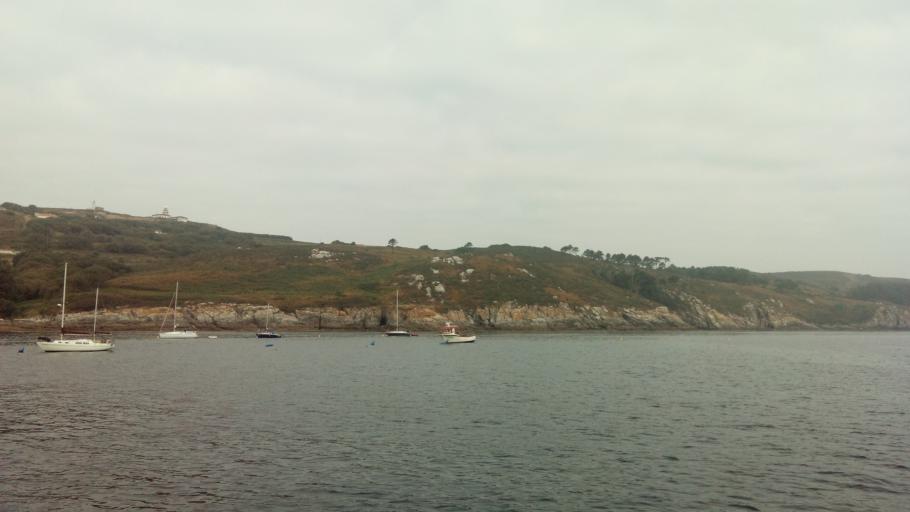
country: ES
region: Galicia
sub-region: Provincia de Pontevedra
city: Sanxenxo
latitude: 42.3778
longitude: -8.9263
